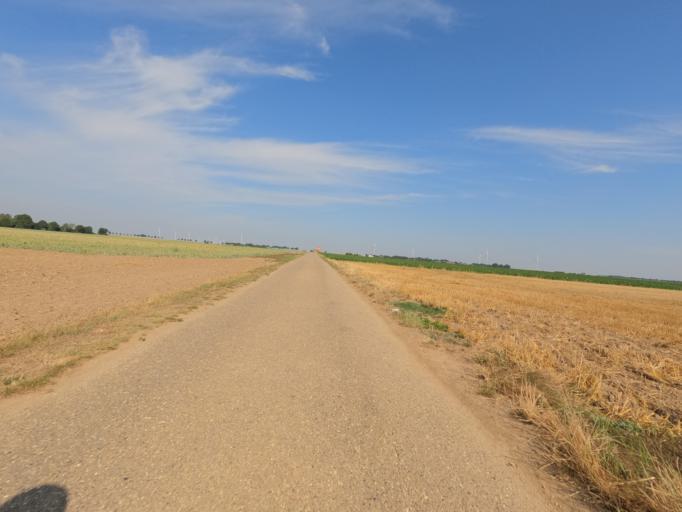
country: DE
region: North Rhine-Westphalia
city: Julich
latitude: 50.9834
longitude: 6.3506
